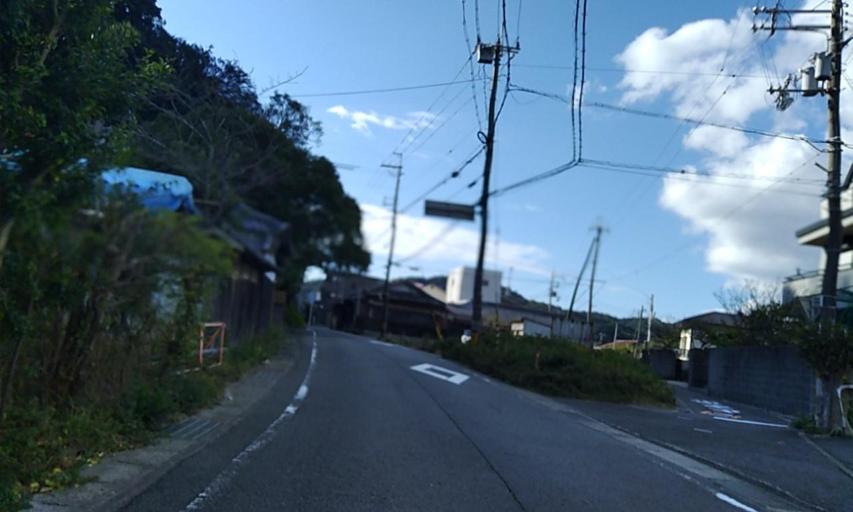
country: JP
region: Wakayama
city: Minato
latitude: 34.2803
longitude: 135.0753
